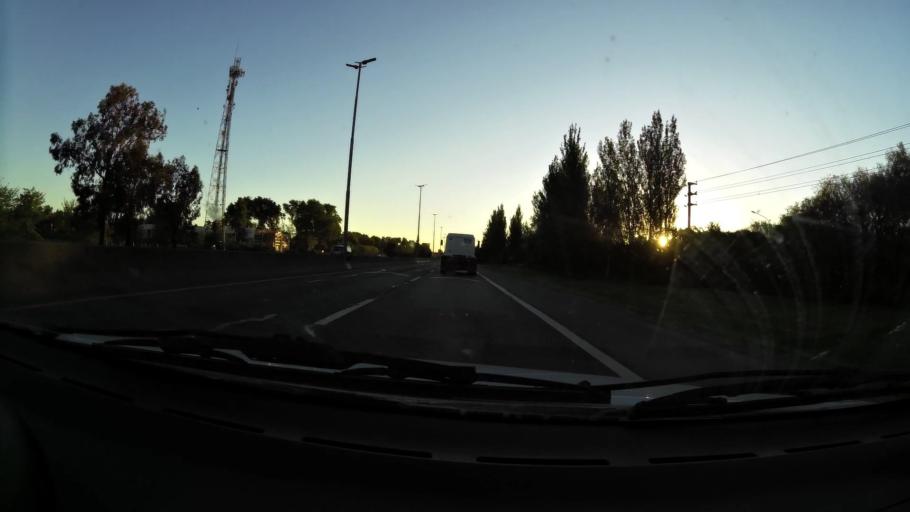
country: AR
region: Buenos Aires
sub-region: Partido de Quilmes
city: Quilmes
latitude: -34.8090
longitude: -58.1741
